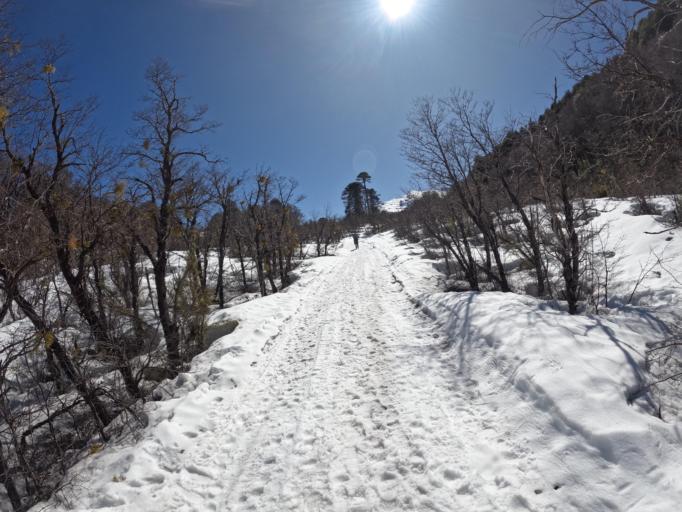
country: CL
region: Araucania
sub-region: Provincia de Cautin
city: Vilcun
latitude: -38.6636
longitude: -71.6192
